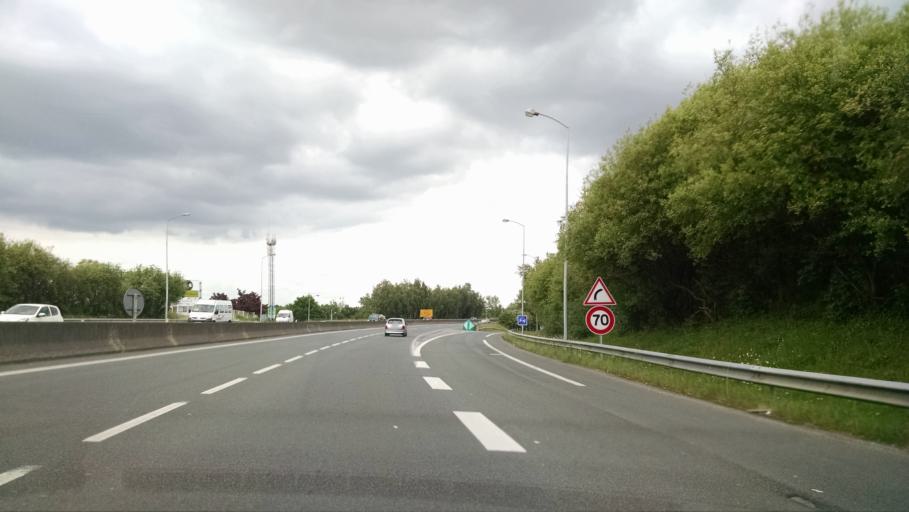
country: FR
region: Pays de la Loire
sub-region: Departement de la Loire-Atlantique
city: Basse-Goulaine
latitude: 47.2097
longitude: -1.4851
